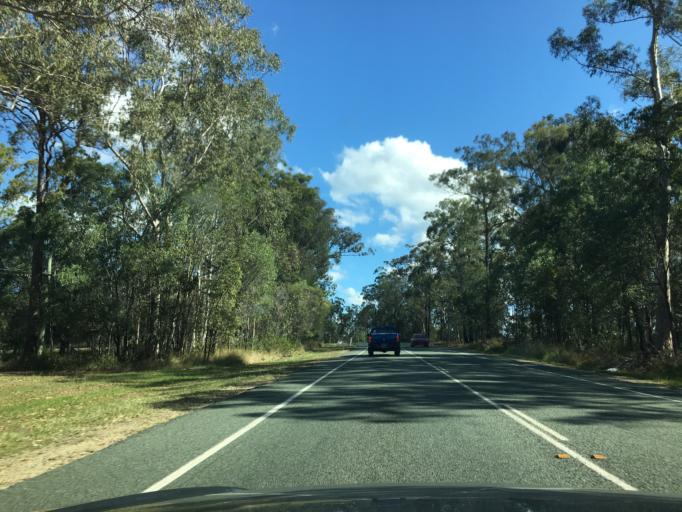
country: AU
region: Queensland
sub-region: Logan
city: Chambers Flat
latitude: -27.7920
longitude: 153.0996
